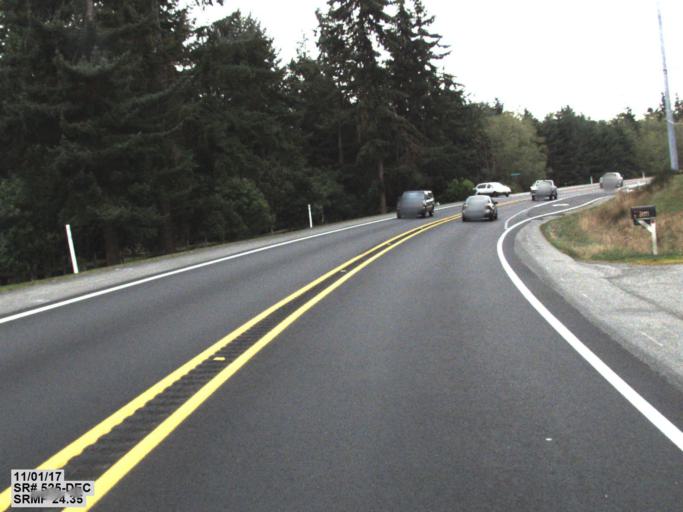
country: US
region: Washington
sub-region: Island County
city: Freeland
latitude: 48.0880
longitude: -122.5682
